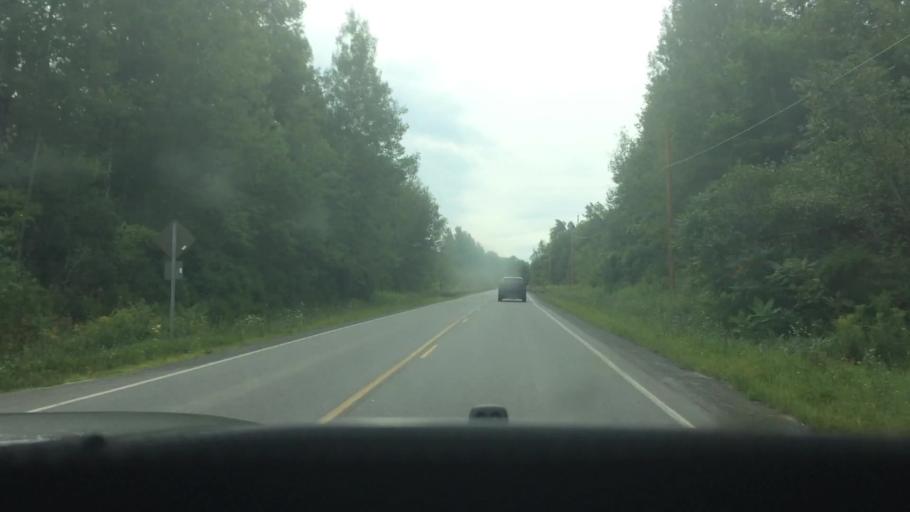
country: US
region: New York
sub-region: St. Lawrence County
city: Canton
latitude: 44.4834
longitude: -75.2469
